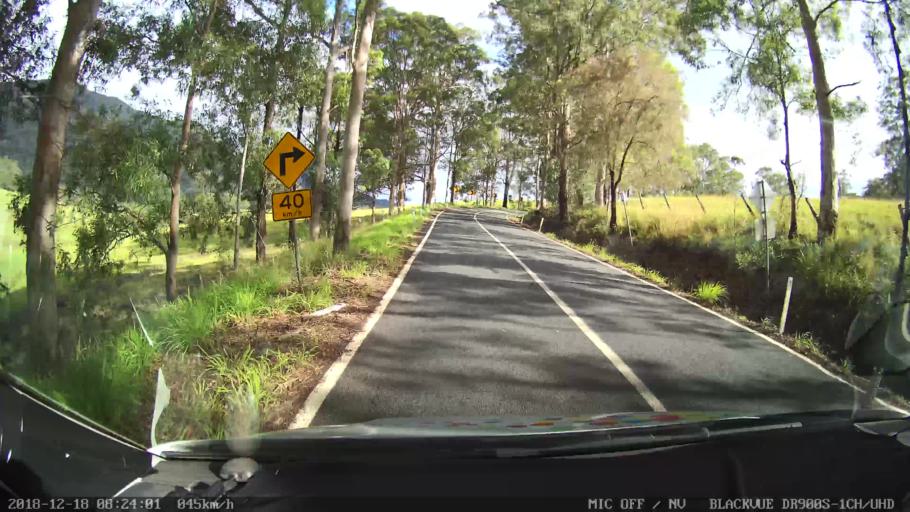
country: AU
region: New South Wales
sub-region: Kyogle
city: Kyogle
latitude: -28.3248
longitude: 152.7324
